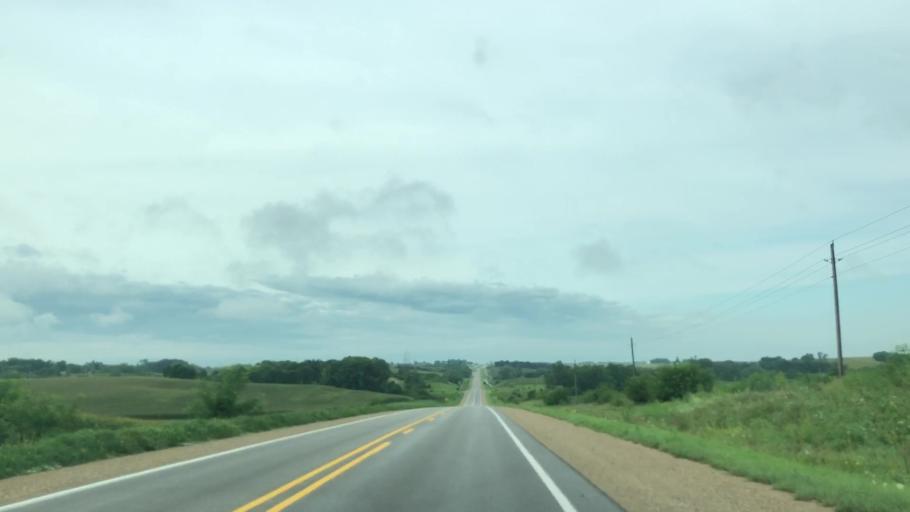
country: US
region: Iowa
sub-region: Marshall County
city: Marshalltown
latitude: 42.0075
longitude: -92.9523
